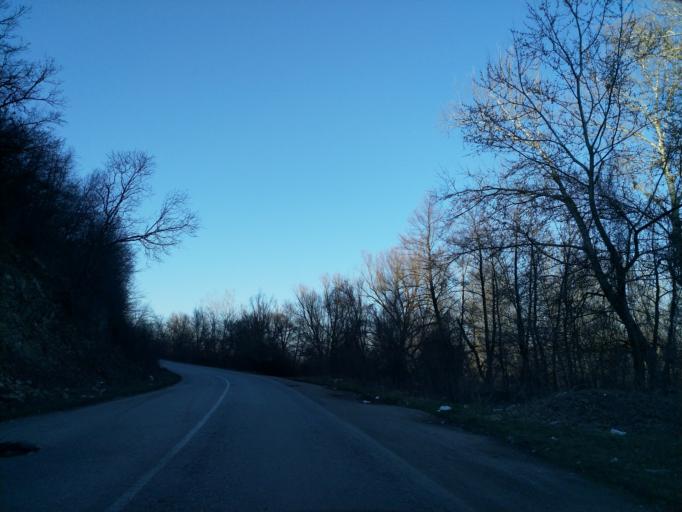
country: RS
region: Central Serbia
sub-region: Pomoravski Okrug
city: Paracin
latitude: 43.8679
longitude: 21.4697
